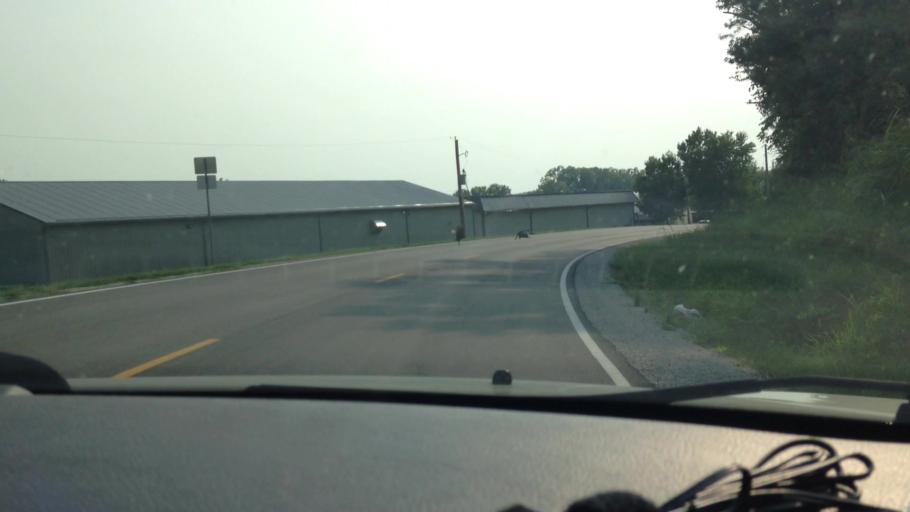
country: US
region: Missouri
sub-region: Platte County
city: Platte City
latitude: 39.3849
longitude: -94.7816
